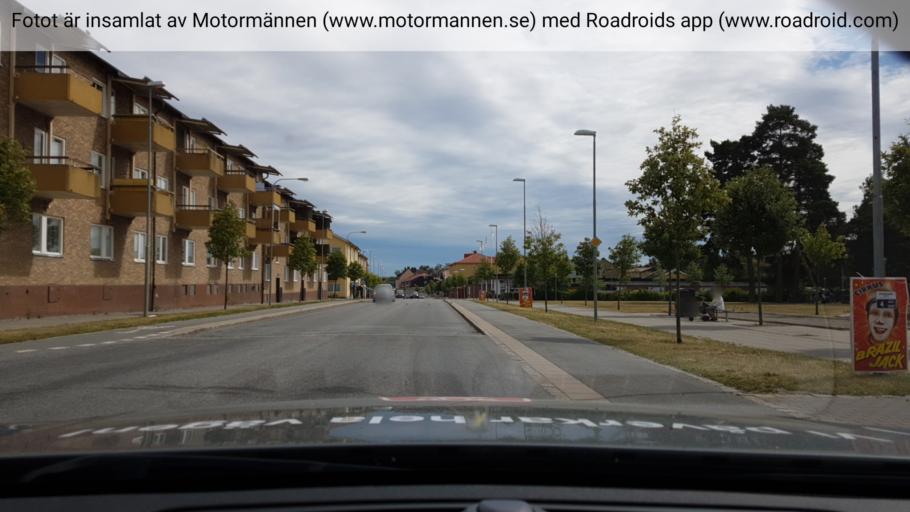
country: SE
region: Stockholm
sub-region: Nynashamns Kommun
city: Nynashamn
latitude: 58.9141
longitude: 17.9465
